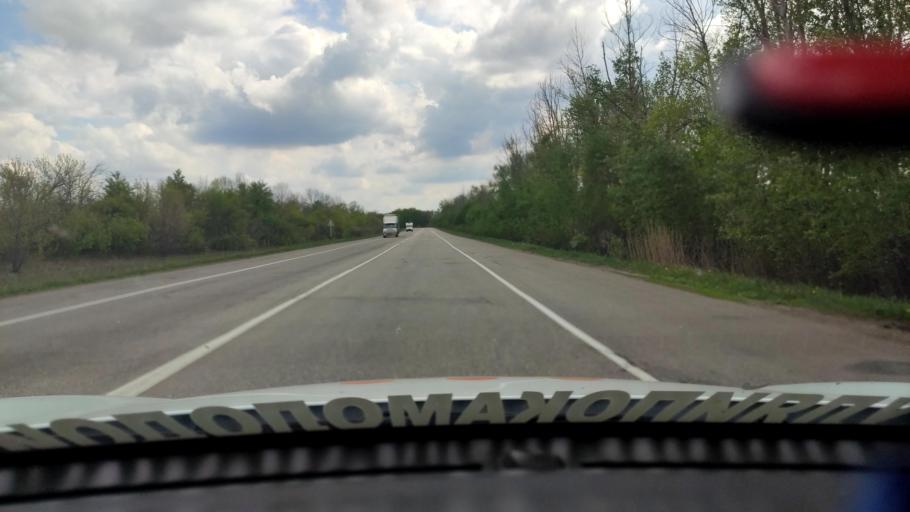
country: RU
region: Voronezj
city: Kolodeznyy
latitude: 51.2919
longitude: 39.0401
